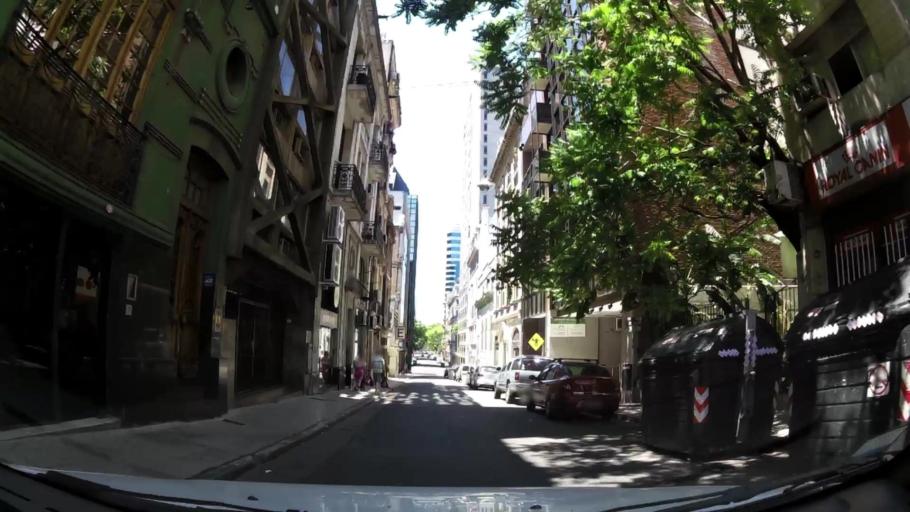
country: AR
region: Buenos Aires F.D.
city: Buenos Aires
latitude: -34.5998
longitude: -58.3723
